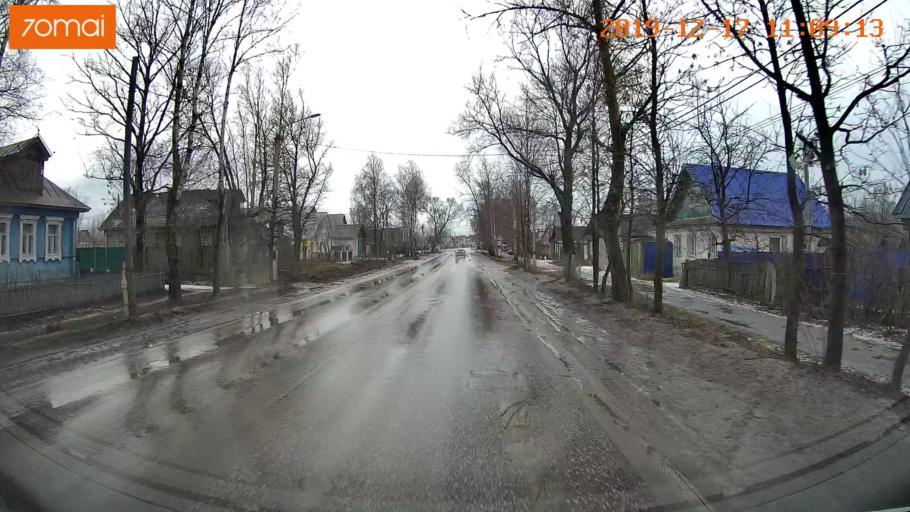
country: RU
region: Vladimir
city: Gus'-Khrustal'nyy
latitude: 55.6023
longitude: 40.6426
